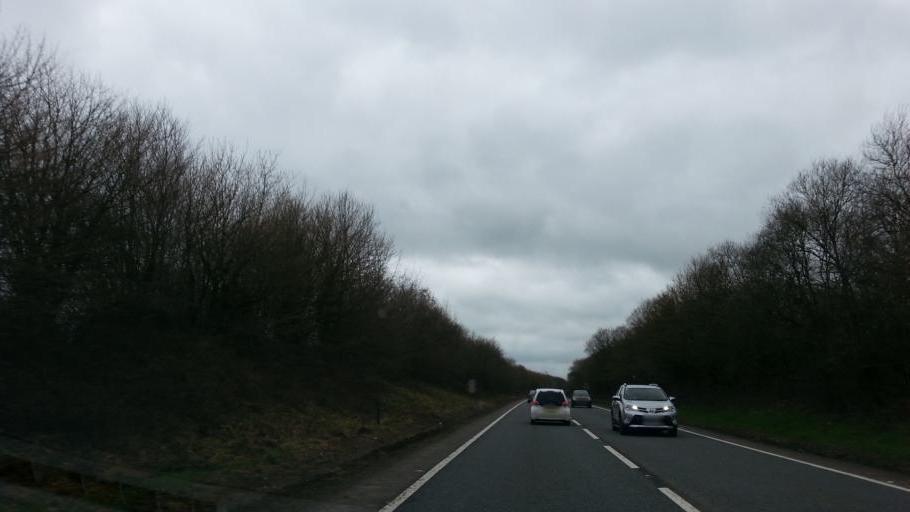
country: GB
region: England
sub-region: Devon
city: Tiverton
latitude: 50.9412
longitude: -3.5804
